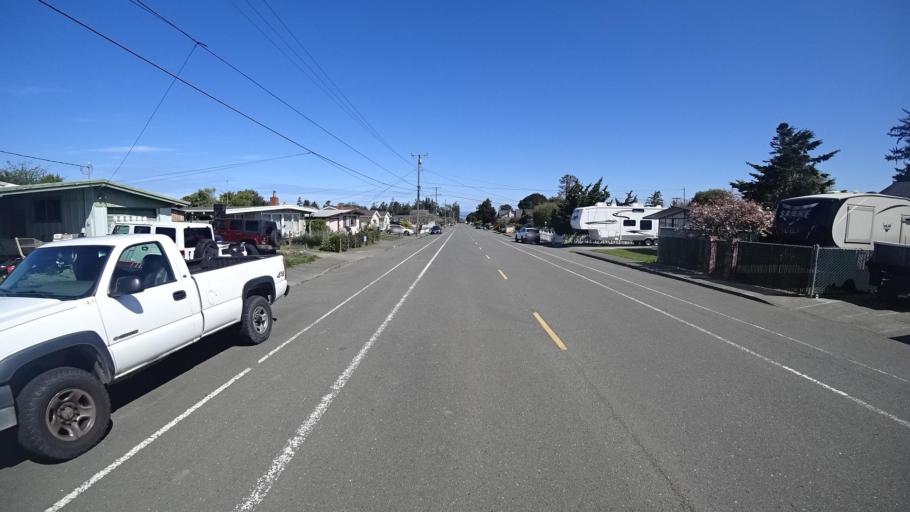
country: US
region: California
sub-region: Humboldt County
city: Myrtletown
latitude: 40.7906
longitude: -124.1262
